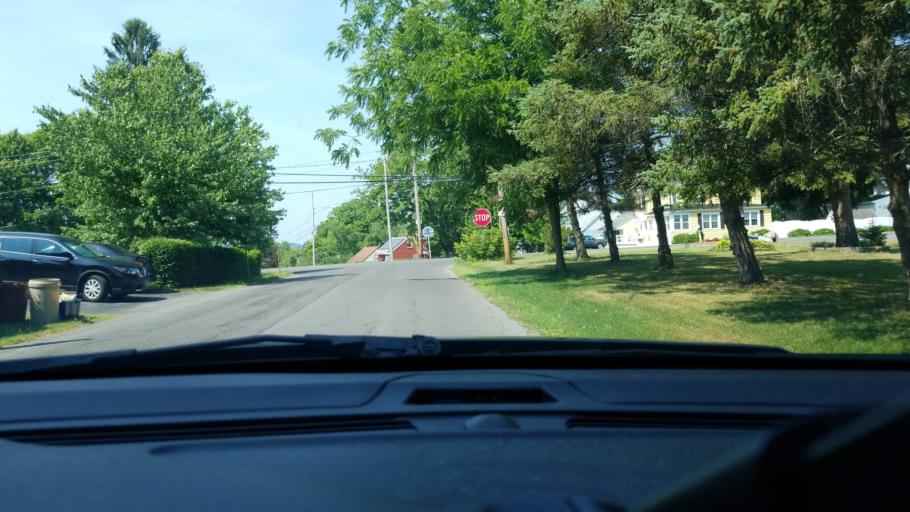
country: US
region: New York
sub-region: Onondaga County
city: Liverpool
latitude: 43.1129
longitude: -76.2213
